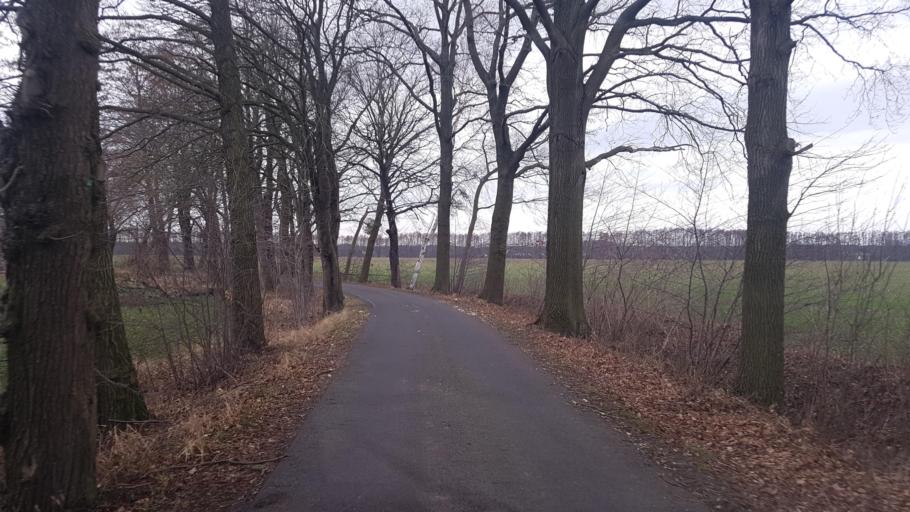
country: DE
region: Brandenburg
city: Drahnsdorf
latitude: 51.9325
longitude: 13.6090
